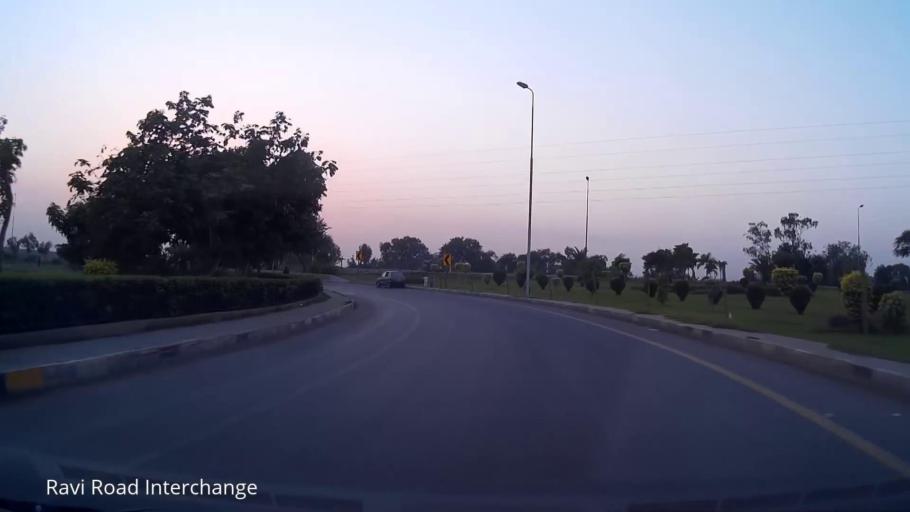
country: PK
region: Punjab
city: Lahore
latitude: 31.6054
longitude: 74.2975
